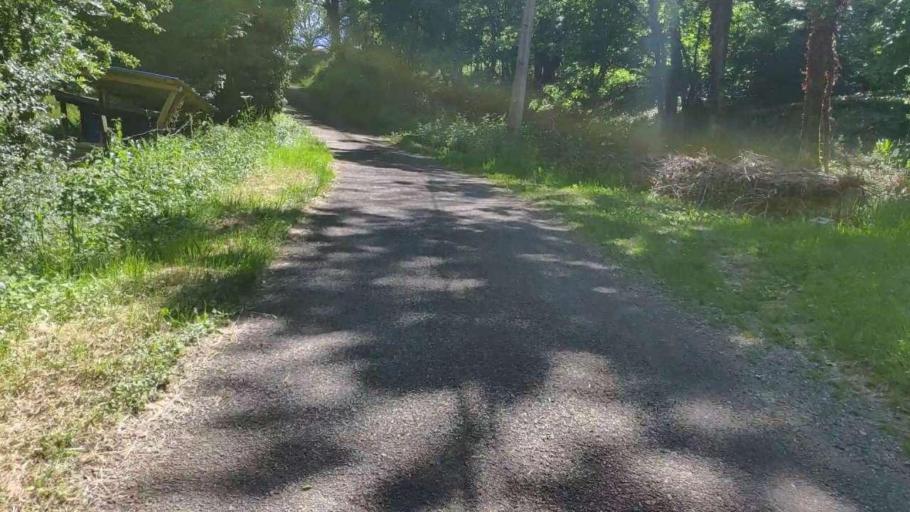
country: FR
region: Franche-Comte
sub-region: Departement du Jura
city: Perrigny
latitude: 46.7323
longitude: 5.6297
